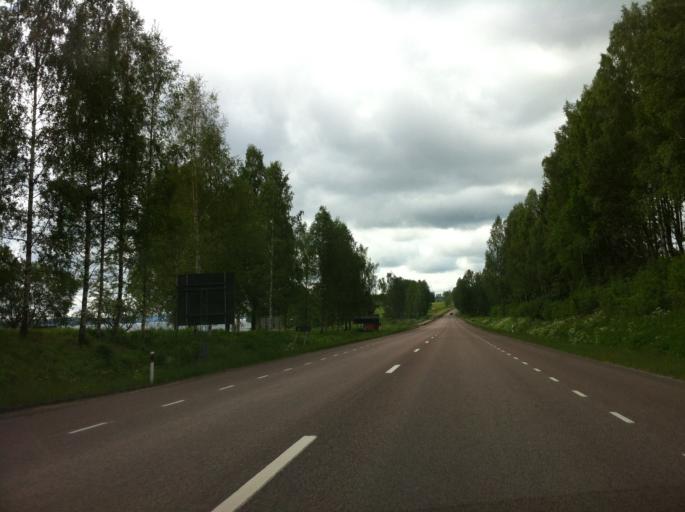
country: SE
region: Vaermland
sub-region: Sunne Kommun
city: Sunne
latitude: 59.8237
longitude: 13.1319
